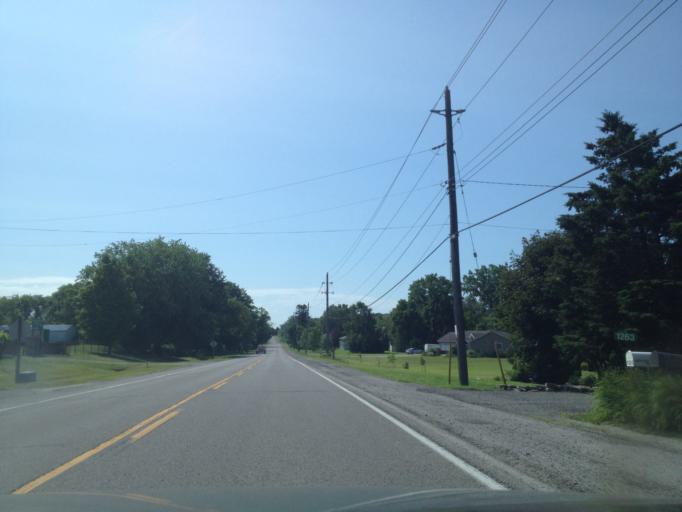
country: CA
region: Ontario
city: Norfolk County
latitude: 42.7631
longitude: -80.3874
